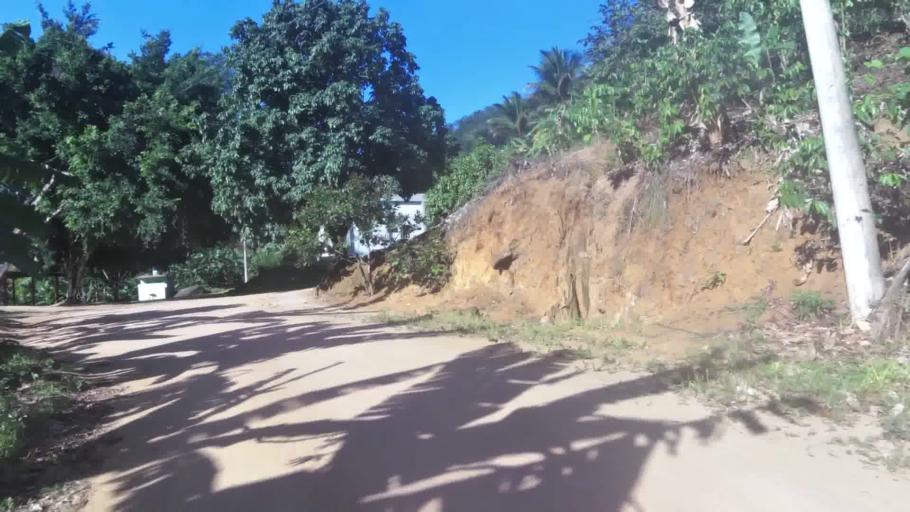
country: BR
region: Espirito Santo
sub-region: Iconha
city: Iconha
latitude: -20.7555
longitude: -40.8121
